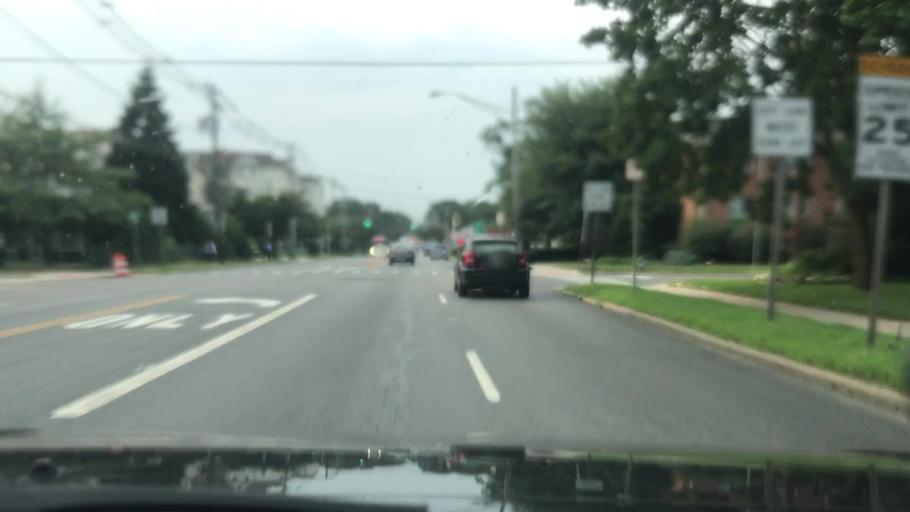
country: US
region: New Jersey
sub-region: Ocean County
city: Lakewood
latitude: 40.0976
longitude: -74.2177
